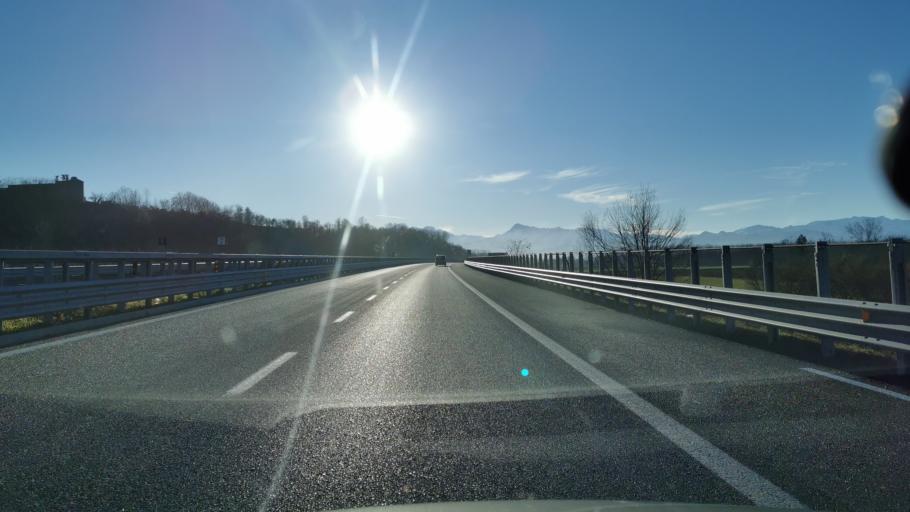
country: IT
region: Piedmont
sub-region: Provincia di Cuneo
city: Castelletto Stura
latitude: 44.4449
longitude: 7.6344
